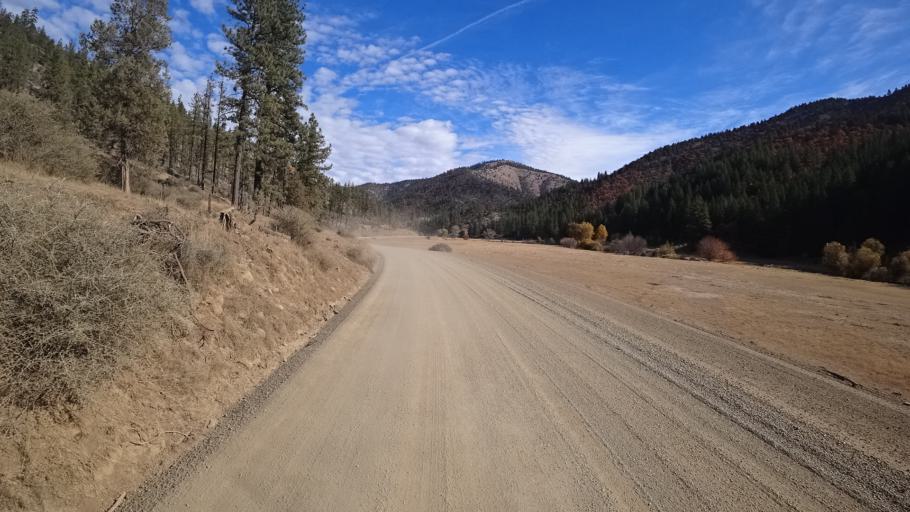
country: US
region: California
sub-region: Siskiyou County
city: Yreka
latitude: 41.6133
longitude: -122.7244
